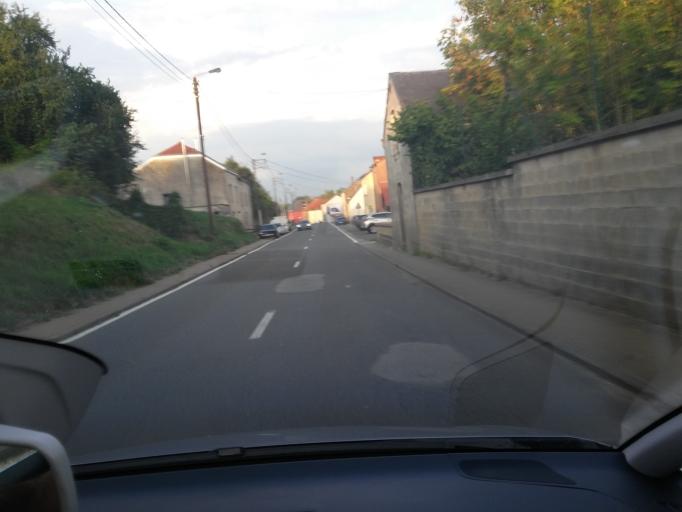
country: BE
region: Wallonia
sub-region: Province du Luxembourg
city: Virton
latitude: 49.5690
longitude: 5.5384
